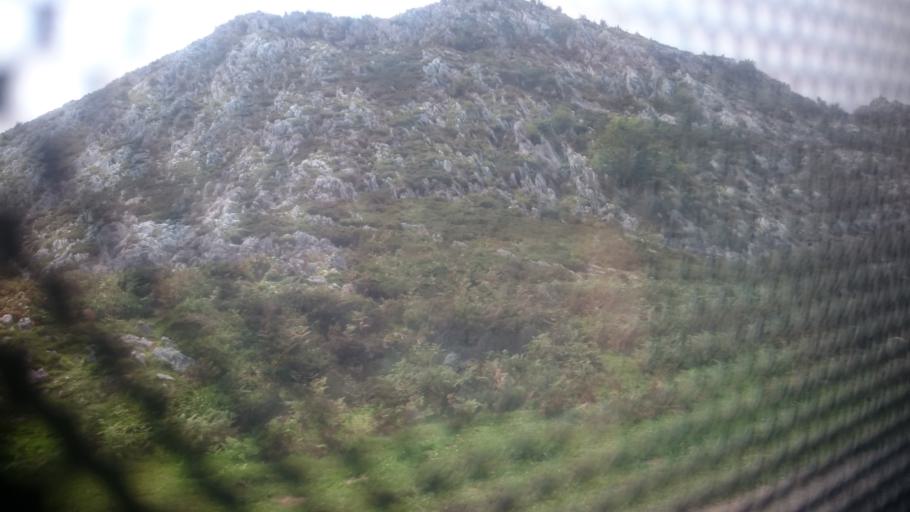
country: ES
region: Asturias
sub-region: Province of Asturias
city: Amieva
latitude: 43.2845
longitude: -5.0085
